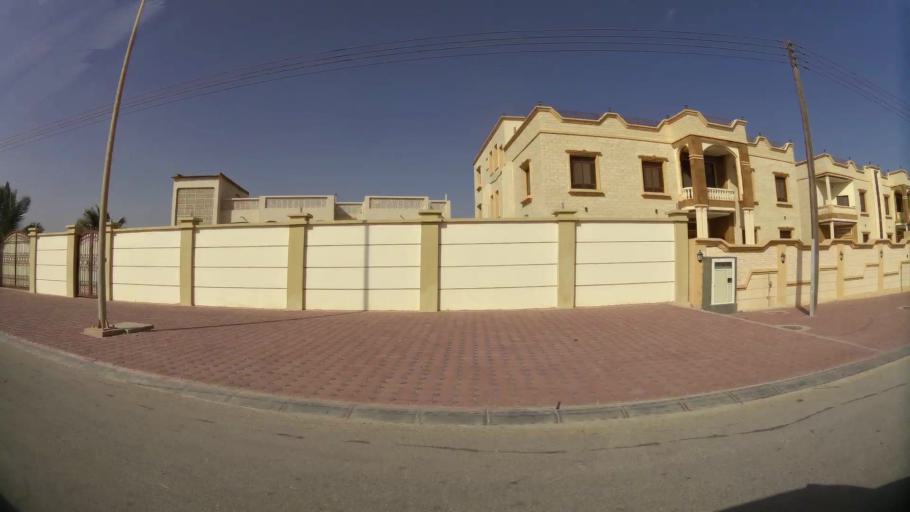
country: OM
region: Zufar
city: Salalah
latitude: 17.0029
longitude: 54.0217
